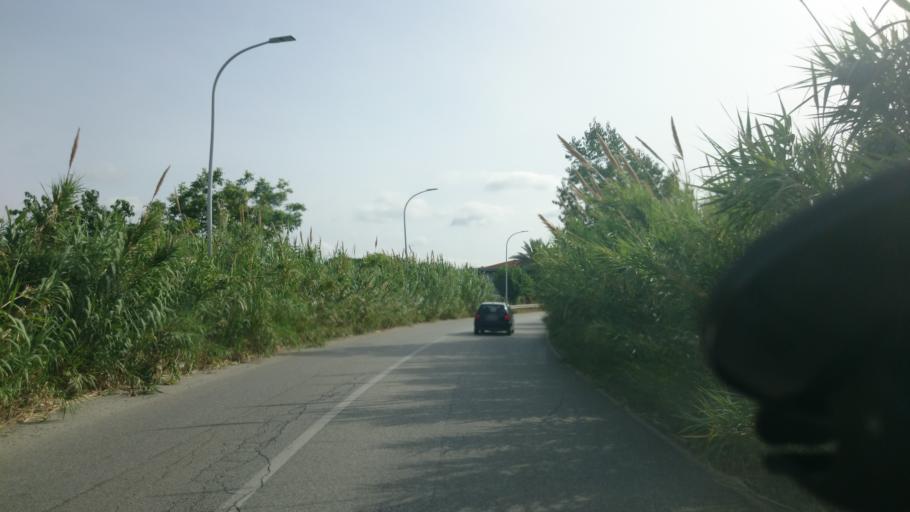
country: IT
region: Calabria
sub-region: Provincia di Vibo-Valentia
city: Pannaconi
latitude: 38.7103
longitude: 16.0772
